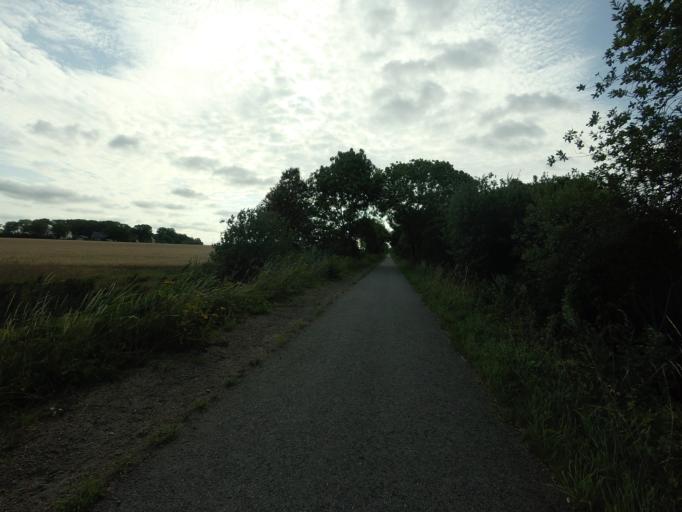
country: SE
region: Skane
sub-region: Hoganas Kommun
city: Hoganas
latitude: 56.1817
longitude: 12.6562
